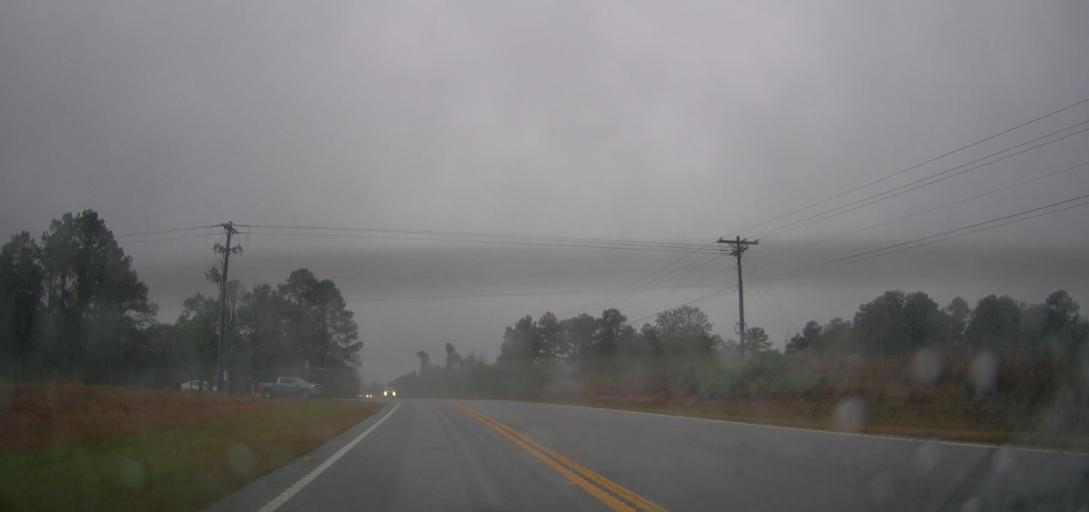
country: US
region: Georgia
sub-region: Jones County
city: Gray
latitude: 33.0381
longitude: -83.5151
